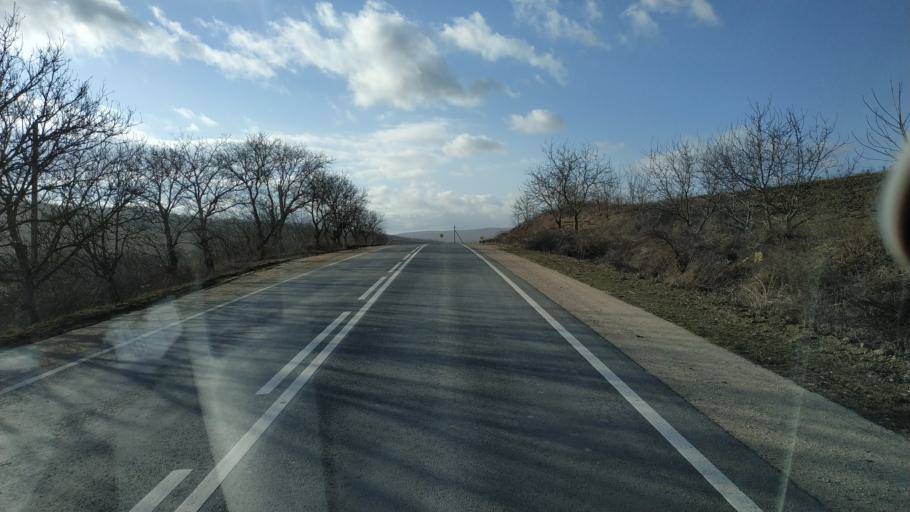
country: MD
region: Calarasi
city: Calarasi
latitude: 47.2968
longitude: 28.1548
